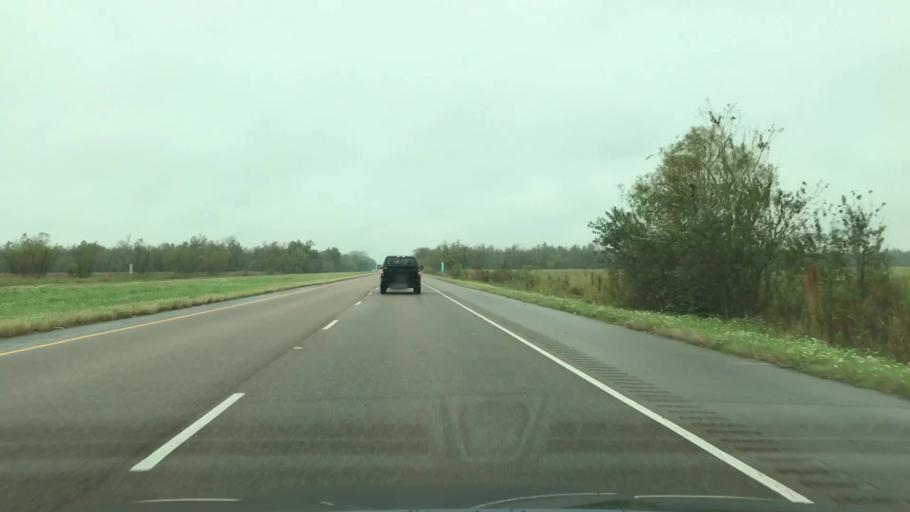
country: US
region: Louisiana
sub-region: Terrebonne Parish
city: Bayou Cane
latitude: 29.6878
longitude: -90.6871
